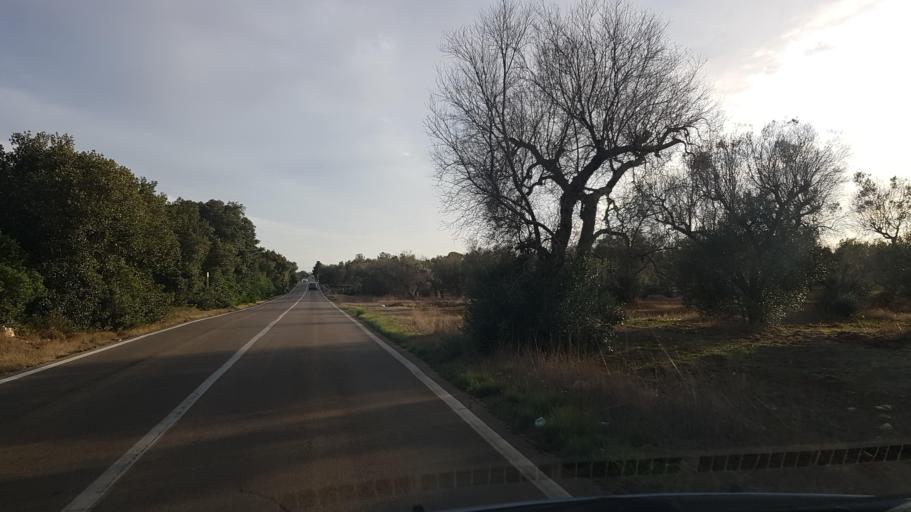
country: IT
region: Apulia
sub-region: Provincia di Brindisi
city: Torchiarolo
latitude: 40.4784
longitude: 18.1242
